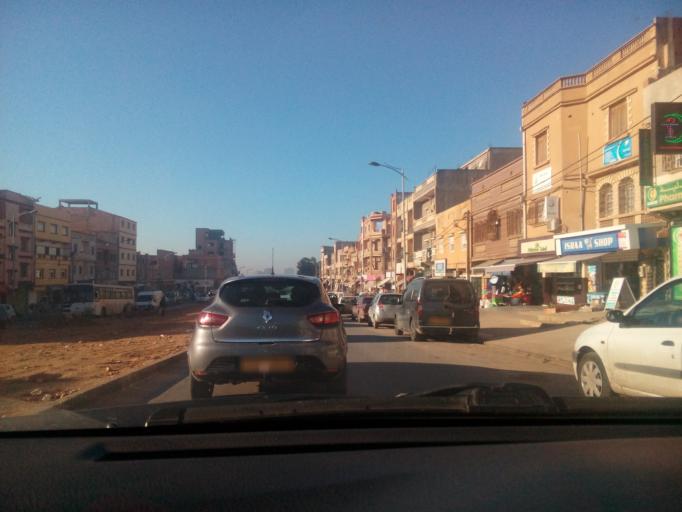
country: DZ
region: Oran
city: Bir el Djir
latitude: 35.7457
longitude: -0.5603
